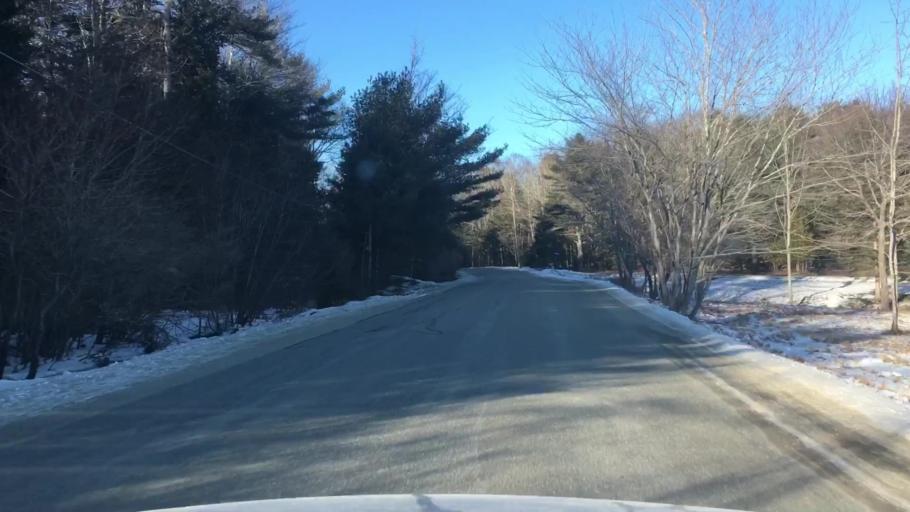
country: US
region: Maine
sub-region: Hancock County
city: Castine
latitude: 44.3420
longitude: -68.7832
